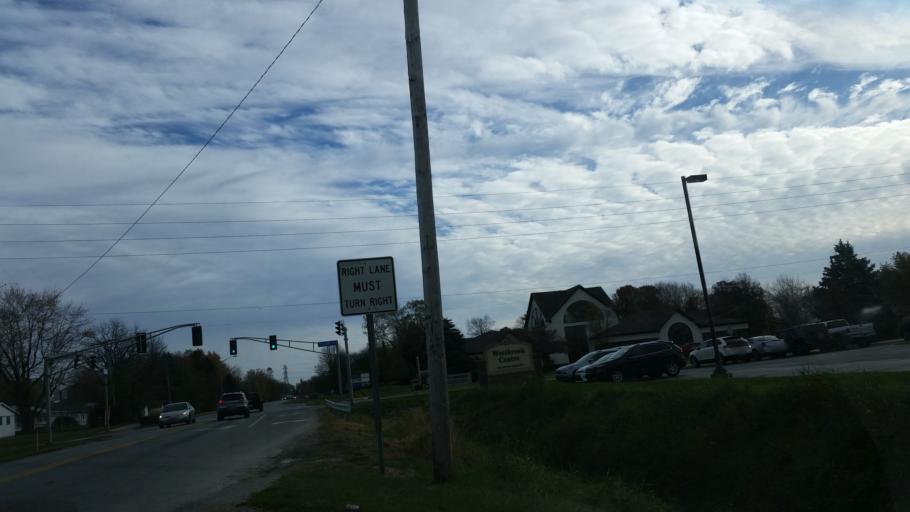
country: US
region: Indiana
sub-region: Howard County
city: Kokomo
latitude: 40.4547
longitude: -86.1563
